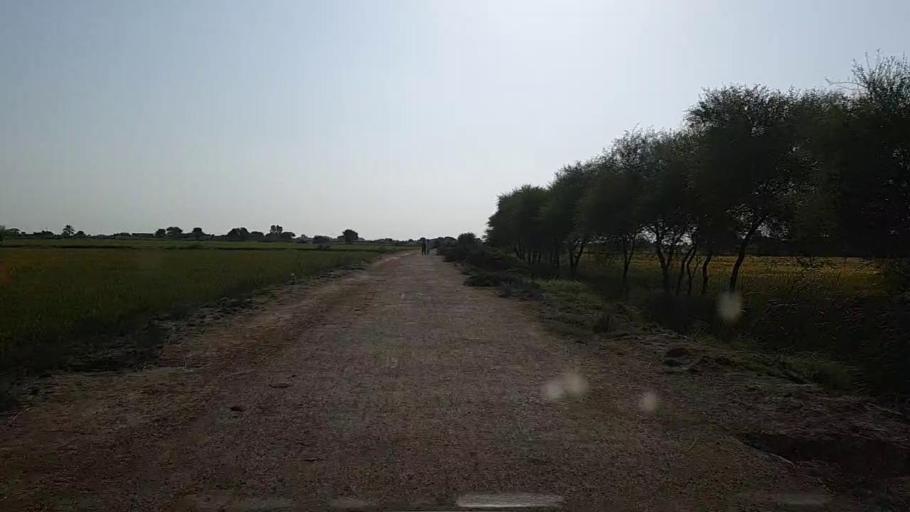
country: PK
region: Sindh
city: Kario
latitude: 24.8230
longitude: 68.4928
